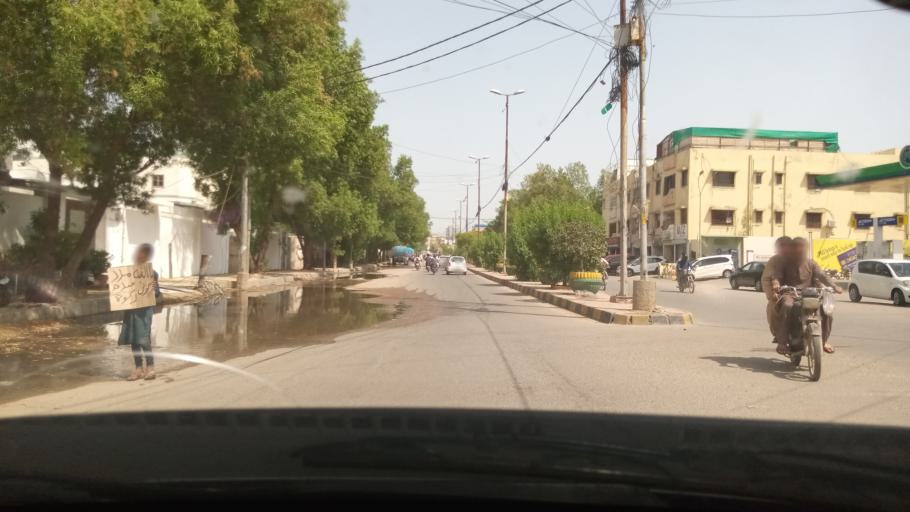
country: PK
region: Sindh
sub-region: Karachi District
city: Karachi
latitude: 24.8754
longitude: 67.0458
